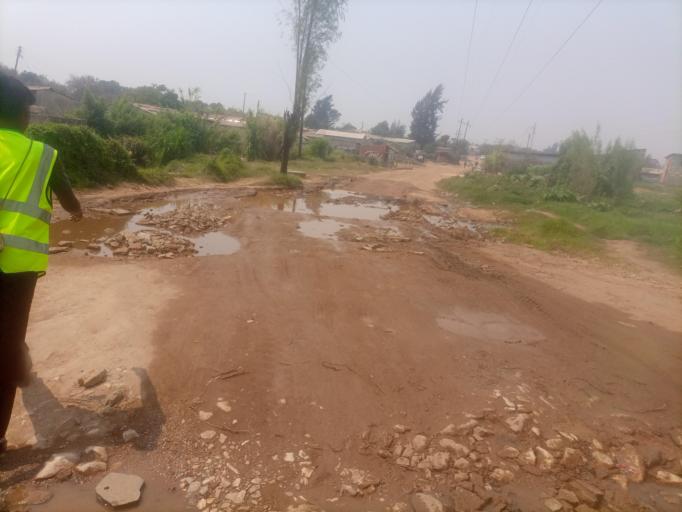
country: ZM
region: Lusaka
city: Lusaka
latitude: -15.3939
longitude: 28.3677
